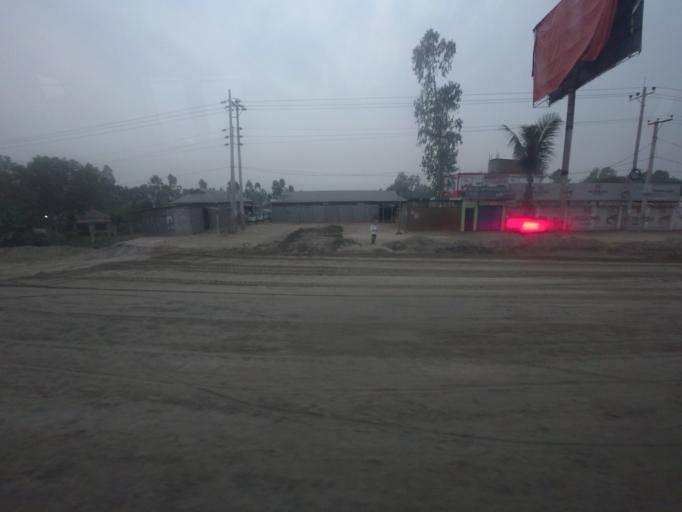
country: BD
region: Dhaka
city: Tangail
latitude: 24.3296
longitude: 89.9249
